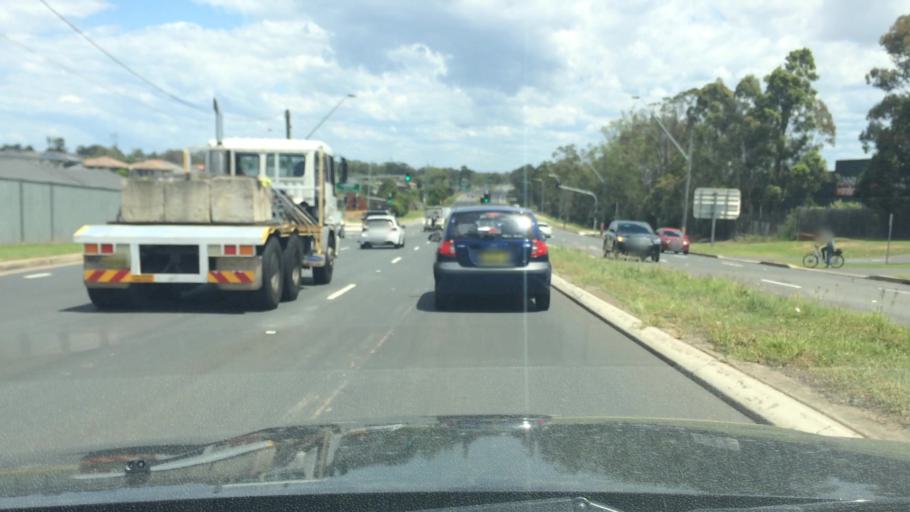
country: AU
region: New South Wales
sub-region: Campbelltown Municipality
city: Glenfield
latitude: -33.9588
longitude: 150.8862
